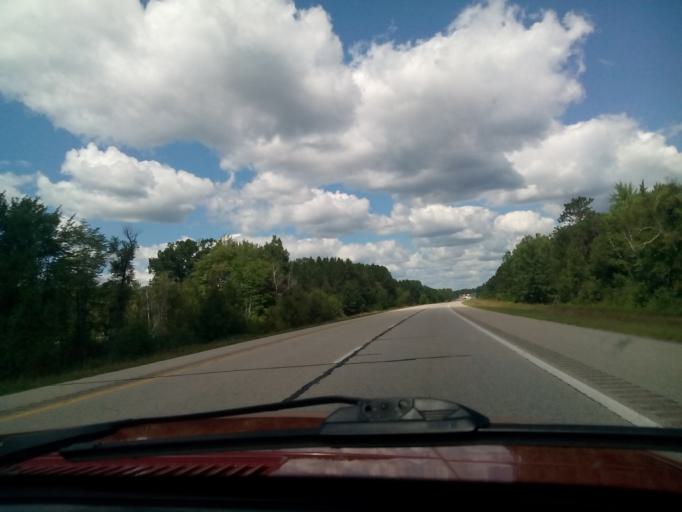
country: US
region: Michigan
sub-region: Ogemaw County
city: Skidway Lake
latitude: 44.1083
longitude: -84.1168
